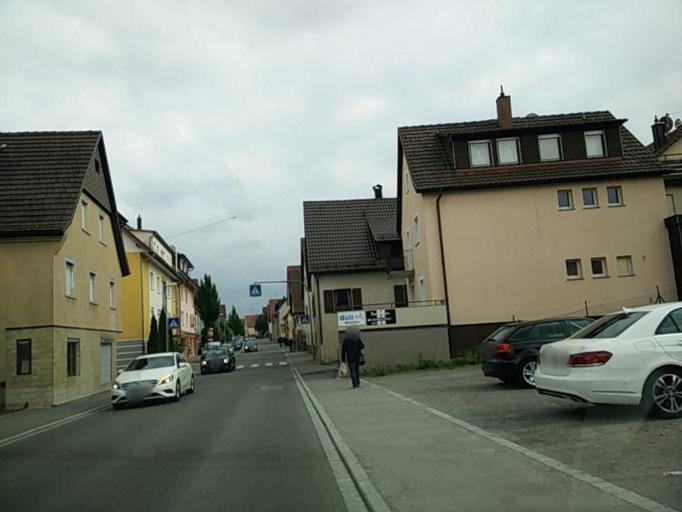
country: DE
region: Baden-Wuerttemberg
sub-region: Regierungsbezirk Stuttgart
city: Holzgerlingen
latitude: 48.6367
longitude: 9.0118
